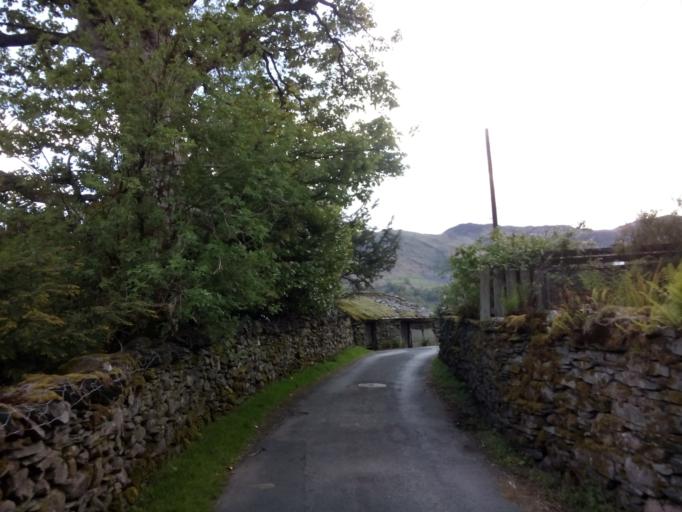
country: GB
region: England
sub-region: Cumbria
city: Ambleside
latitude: 54.4411
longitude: -3.0442
